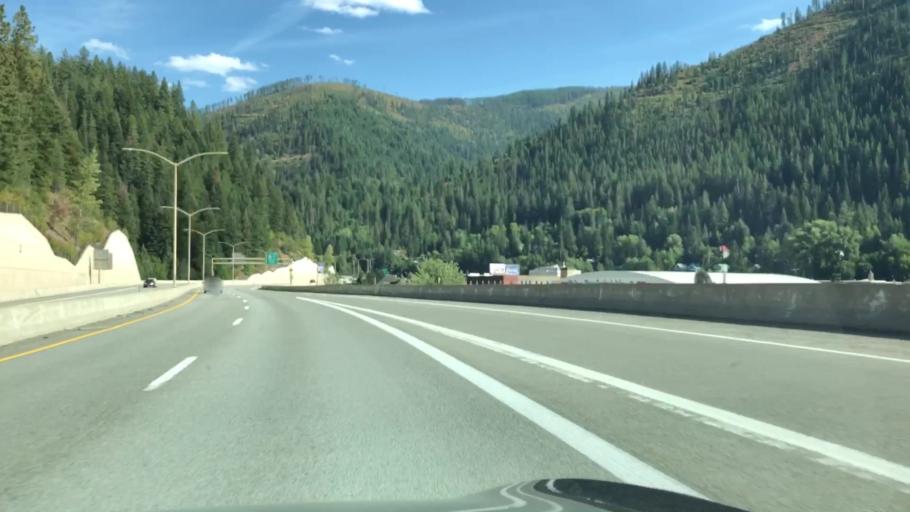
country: US
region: Idaho
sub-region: Shoshone County
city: Wallace
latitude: 47.4750
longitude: -115.9275
